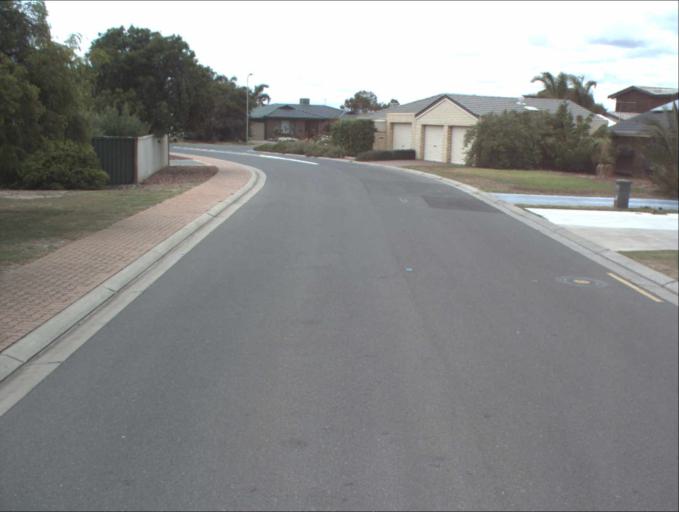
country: AU
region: South Australia
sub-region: Port Adelaide Enfield
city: Birkenhead
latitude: -34.7861
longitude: 138.4966
